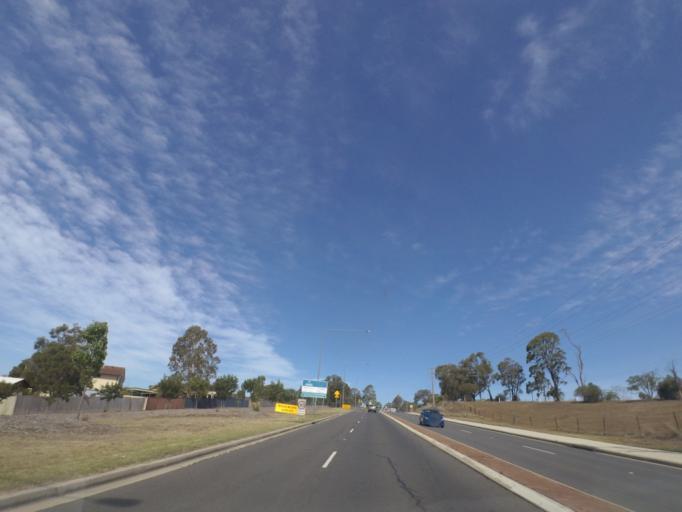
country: AU
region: New South Wales
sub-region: Campbelltown Municipality
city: Campbelltown
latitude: -34.0457
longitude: 150.8006
